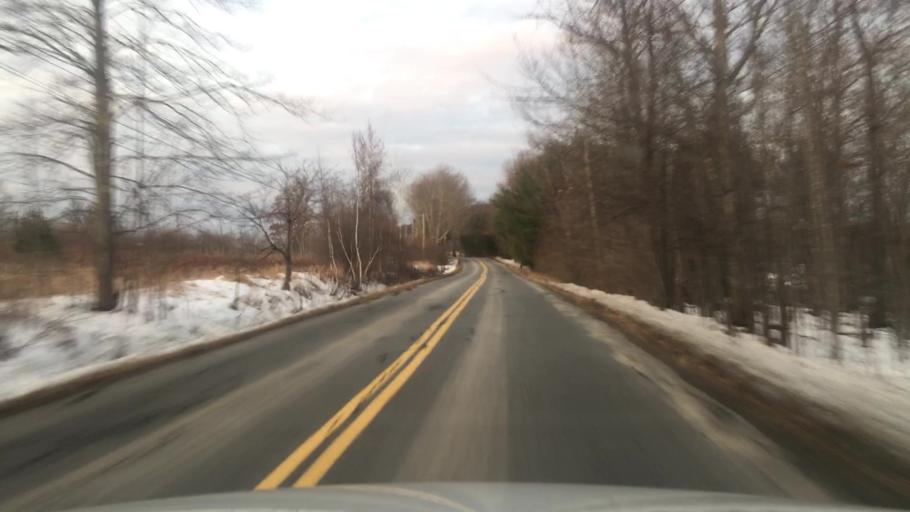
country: US
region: Maine
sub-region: Somerset County
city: Canaan
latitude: 44.7507
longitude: -69.6296
